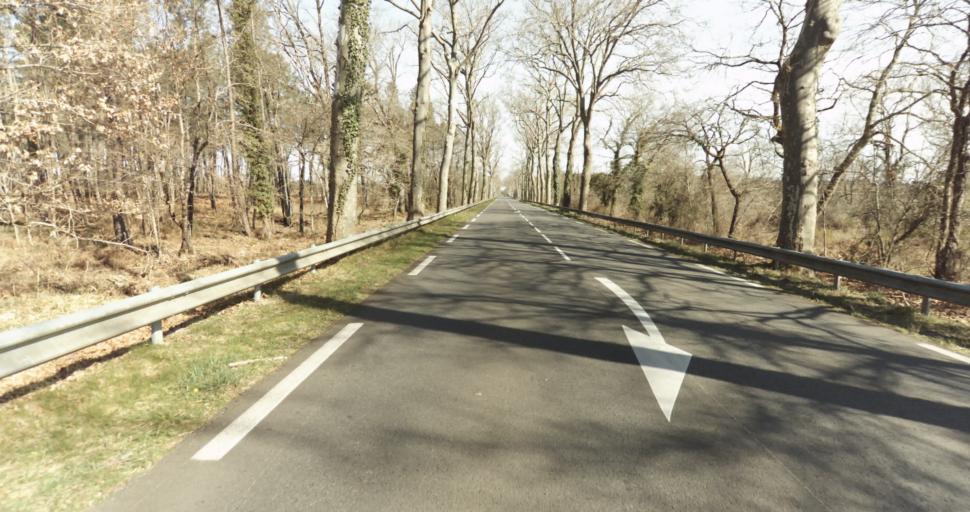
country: FR
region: Aquitaine
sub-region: Departement des Landes
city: Roquefort
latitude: 44.0838
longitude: -0.3112
